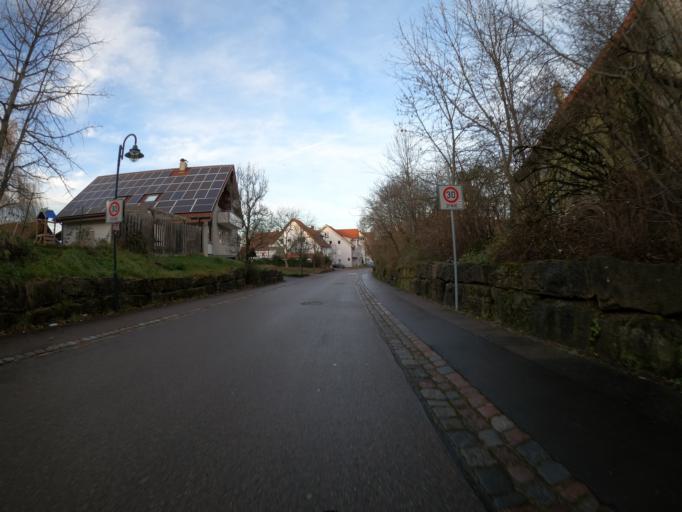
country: DE
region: Baden-Wuerttemberg
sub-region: Regierungsbezirk Stuttgart
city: Zell unter Aichelberg
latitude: 48.6478
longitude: 9.5709
